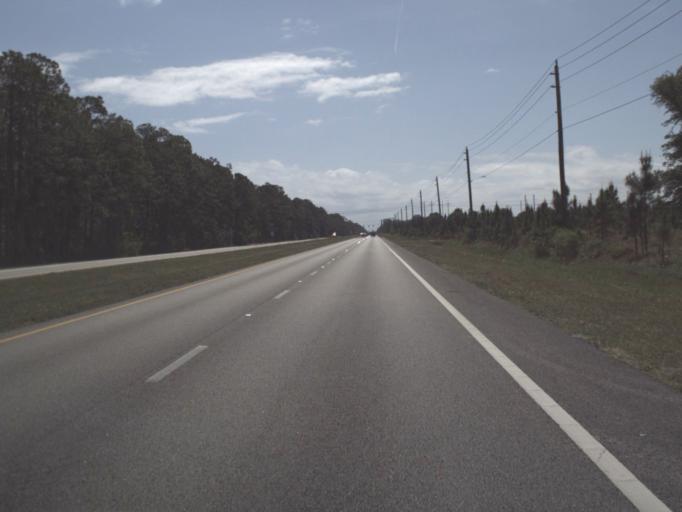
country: US
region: Florida
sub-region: Volusia County
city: Ormond-by-the-Sea
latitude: 29.3589
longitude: -81.1625
